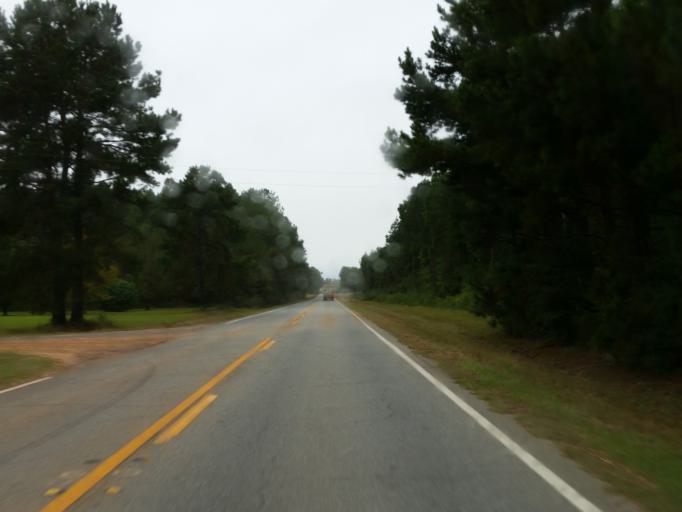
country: US
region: Georgia
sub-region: Berrien County
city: Nashville
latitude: 31.1126
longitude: -83.2996
